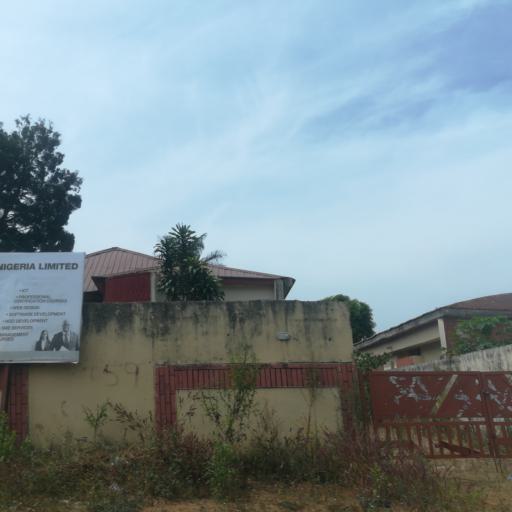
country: NG
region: Plateau
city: Bukuru
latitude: 9.8658
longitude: 8.8521
